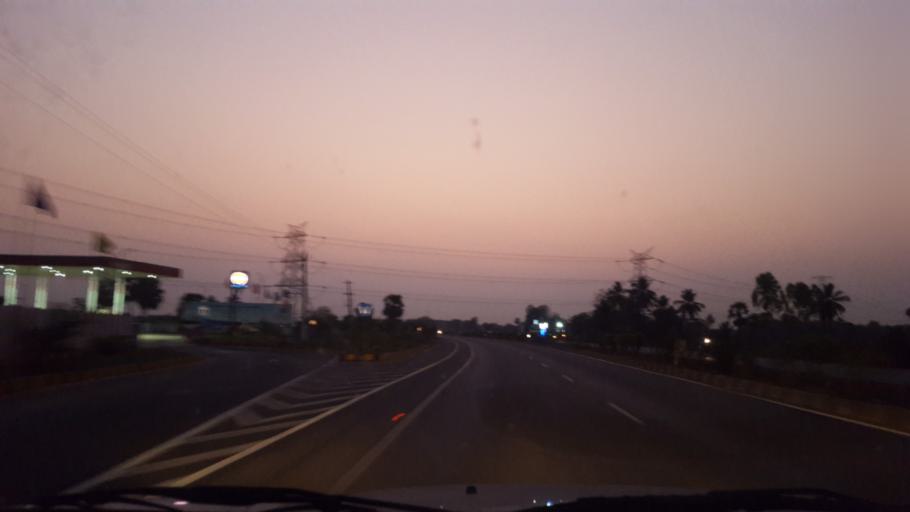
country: IN
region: Andhra Pradesh
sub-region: East Godavari
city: Peddapuram
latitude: 17.1324
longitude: 81.9494
